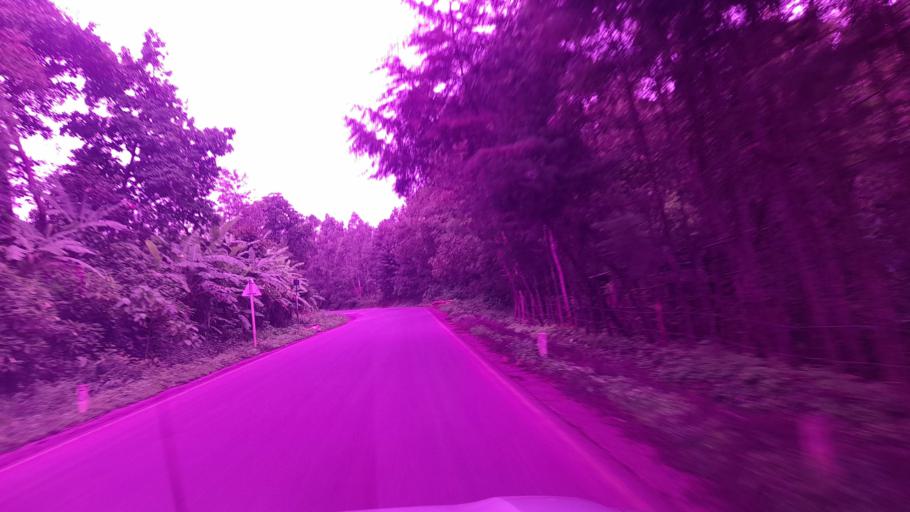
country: ET
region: Oromiya
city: Jima
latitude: 7.6630
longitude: 36.8882
